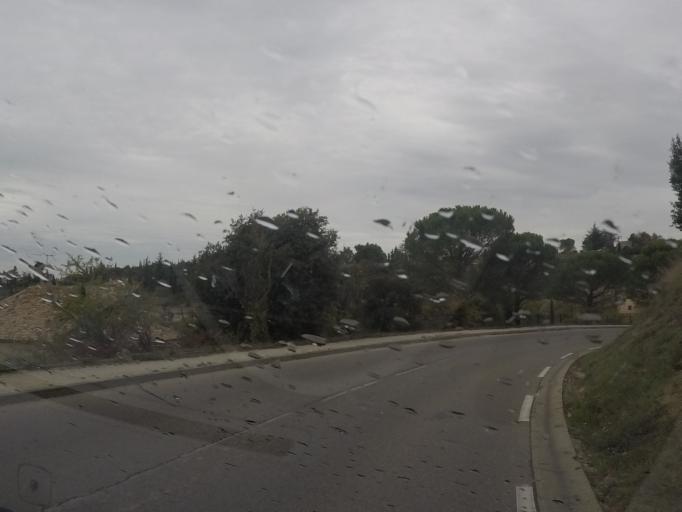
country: FR
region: Provence-Alpes-Cote d'Azur
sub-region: Departement du Vaucluse
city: Bonnieux
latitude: 43.8216
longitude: 5.3154
